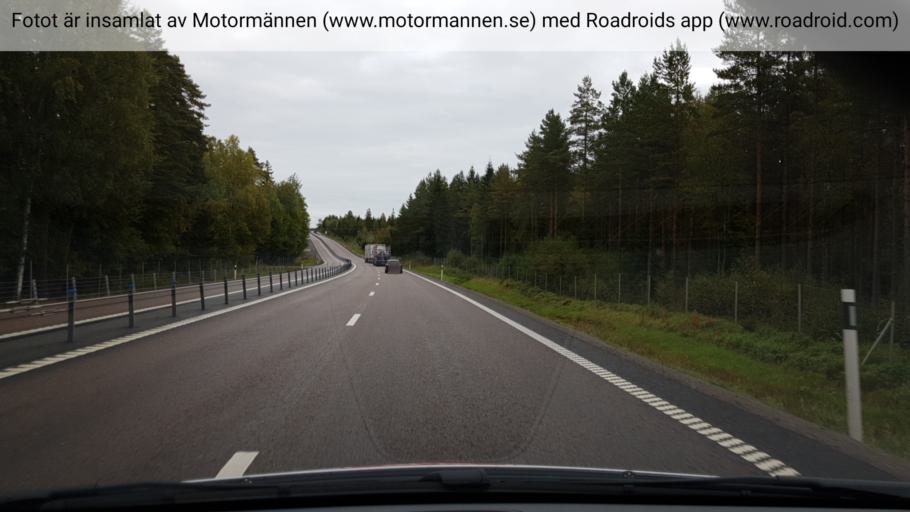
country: SE
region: Vaermland
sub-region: Kristinehamns Kommun
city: Kristinehamn
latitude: 59.3130
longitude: 14.1654
